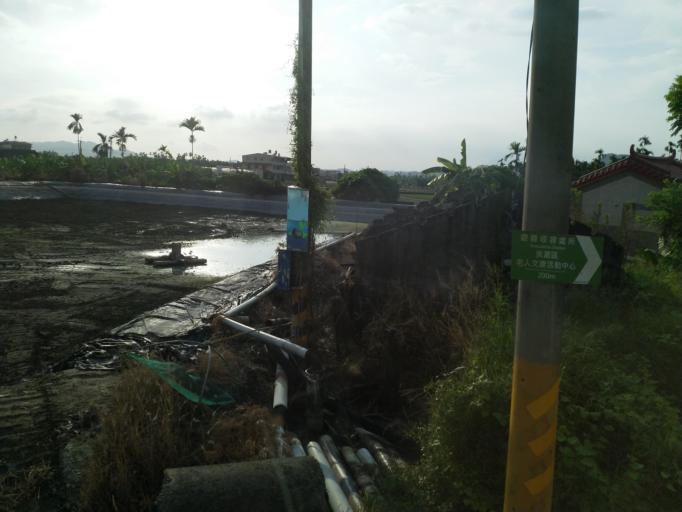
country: TW
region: Taiwan
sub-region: Pingtung
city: Pingtung
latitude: 22.8801
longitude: 120.5353
